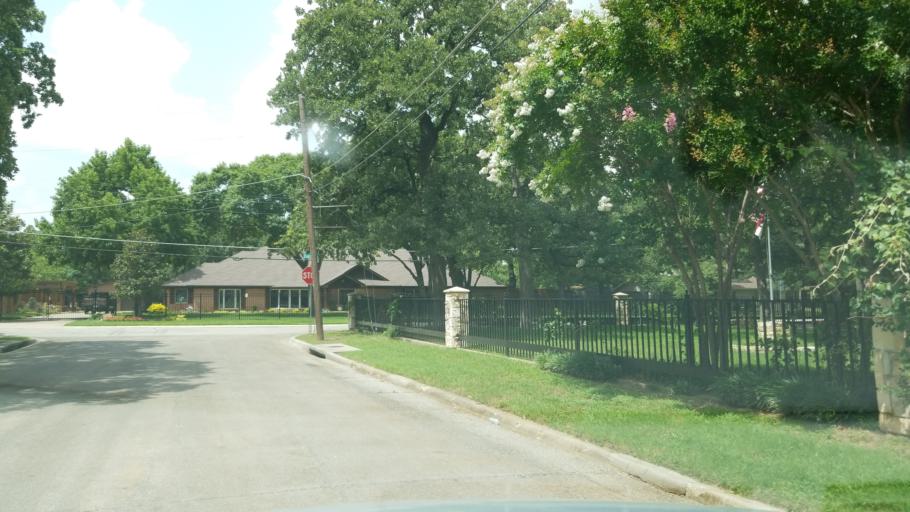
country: US
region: Texas
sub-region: Dallas County
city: Irving
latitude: 32.8258
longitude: -96.9273
